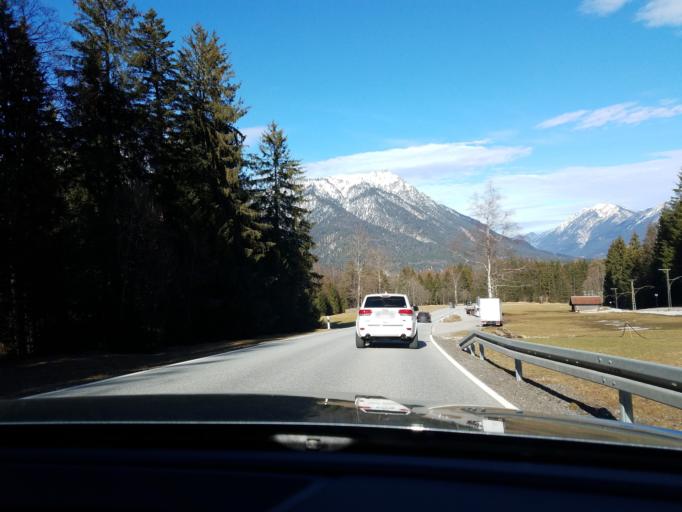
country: DE
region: Bavaria
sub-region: Upper Bavaria
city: Grainau
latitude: 47.4596
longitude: 10.9994
